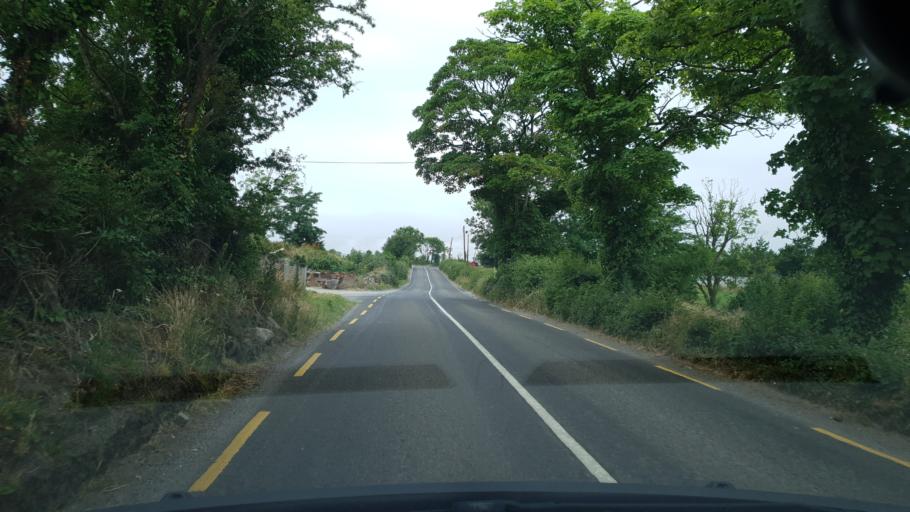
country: IE
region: Munster
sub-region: Ciarrai
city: Tralee
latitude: 52.1587
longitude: -9.6719
